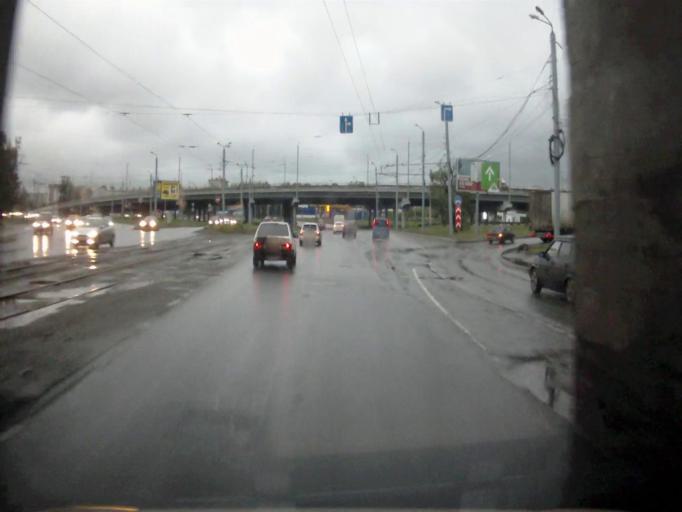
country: RU
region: Chelyabinsk
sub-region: Gorod Chelyabinsk
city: Chelyabinsk
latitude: 55.1521
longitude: 61.4425
